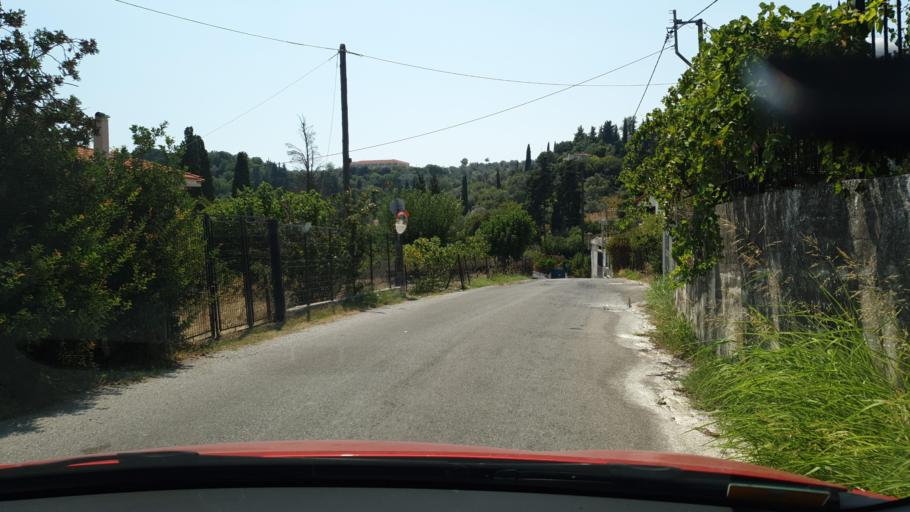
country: GR
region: Central Greece
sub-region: Nomos Evvoias
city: Oxilithos
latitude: 38.5733
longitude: 24.0632
